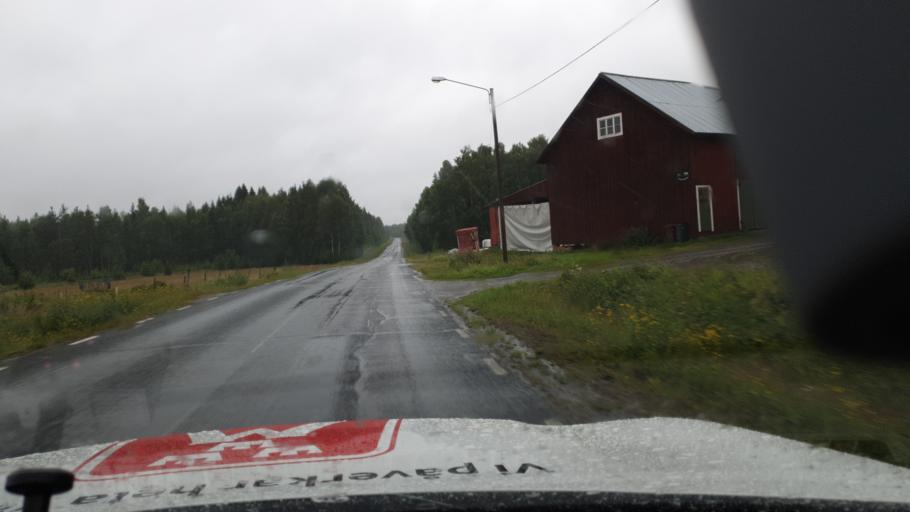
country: SE
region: Vaesterbotten
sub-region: Skelleftea Kommun
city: Soedra Bergsbyn
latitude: 64.5957
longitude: 21.0701
